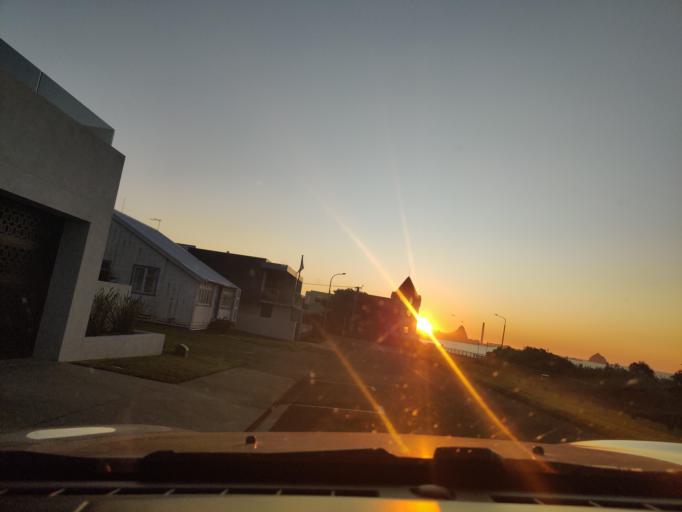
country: NZ
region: Taranaki
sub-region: New Plymouth District
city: New Plymouth
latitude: -39.0517
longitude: 174.0819
